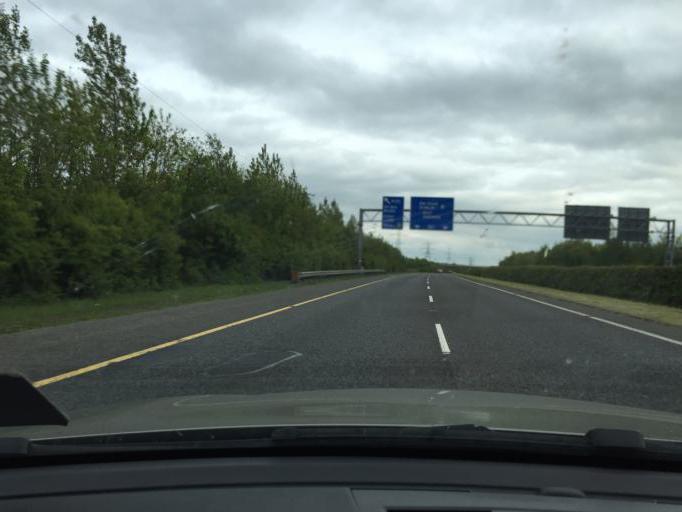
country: IE
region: Leinster
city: Balrothery
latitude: 53.5823
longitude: -6.2106
